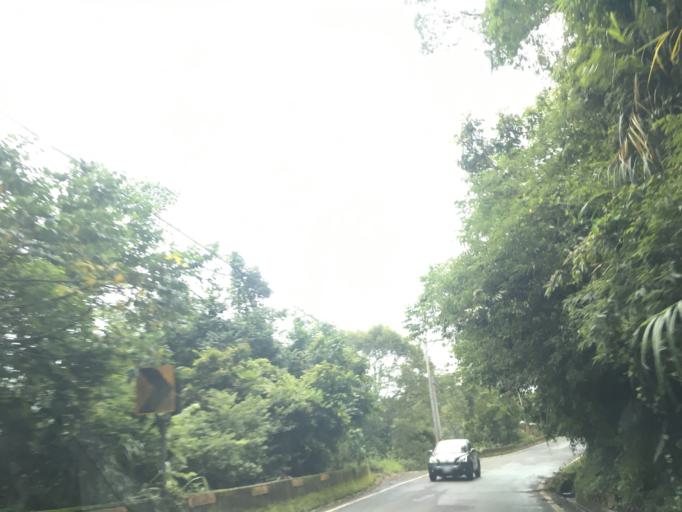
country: TW
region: Taiwan
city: Lugu
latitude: 23.5337
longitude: 120.7029
